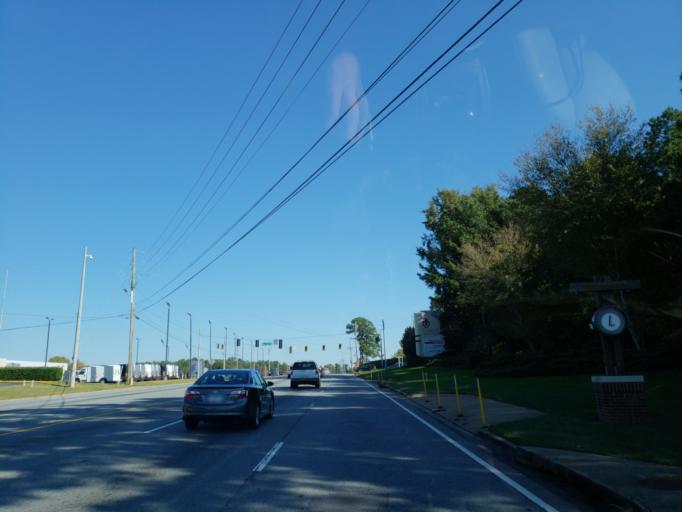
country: US
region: Georgia
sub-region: Gwinnett County
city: Lawrenceville
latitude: 33.9667
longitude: -84.0142
